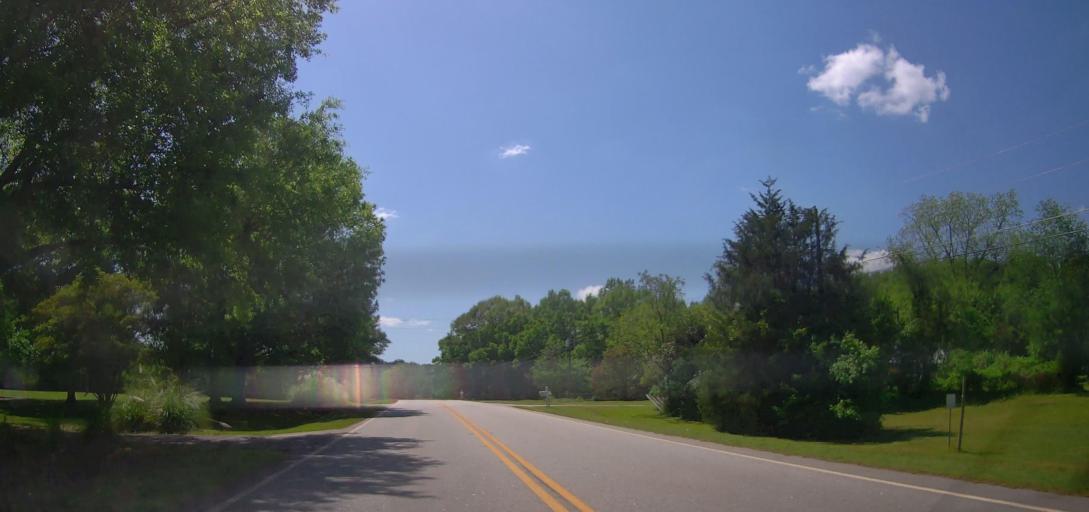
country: US
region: Georgia
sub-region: Putnam County
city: Eatonton
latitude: 33.3399
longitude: -83.3566
